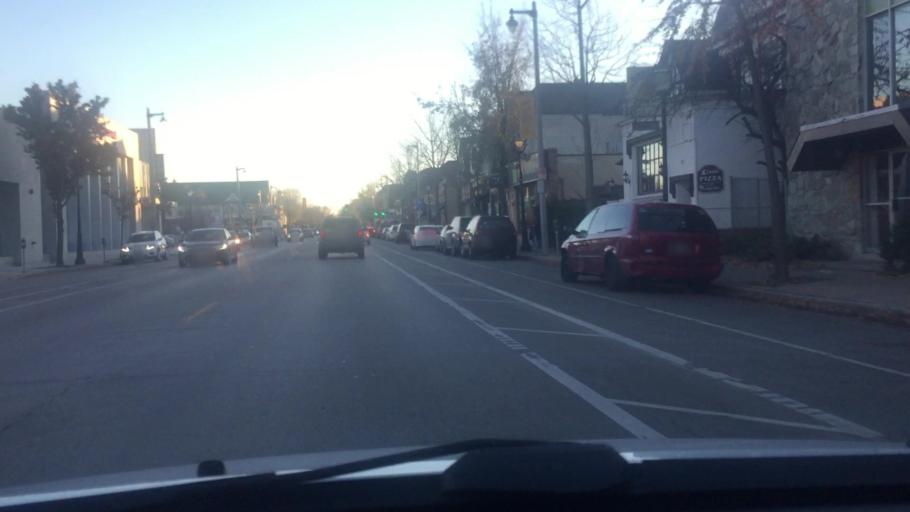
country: US
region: Wisconsin
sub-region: Milwaukee County
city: Shorewood
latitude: 43.0726
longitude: -87.8880
